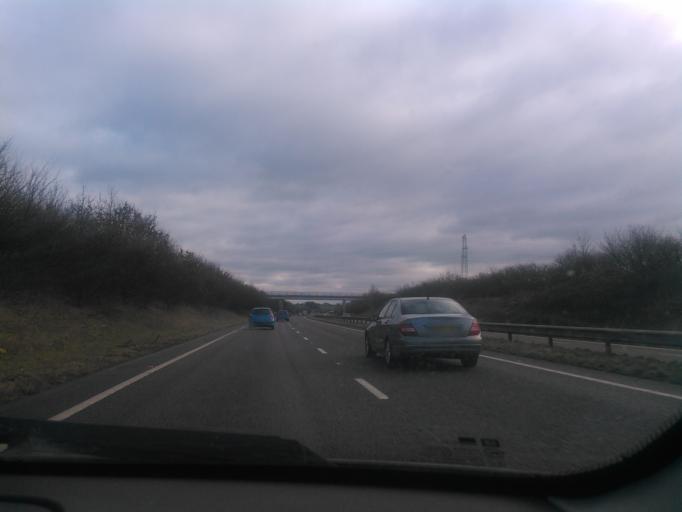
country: GB
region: England
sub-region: Derbyshire
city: Findern
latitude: 52.8687
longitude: -1.5023
